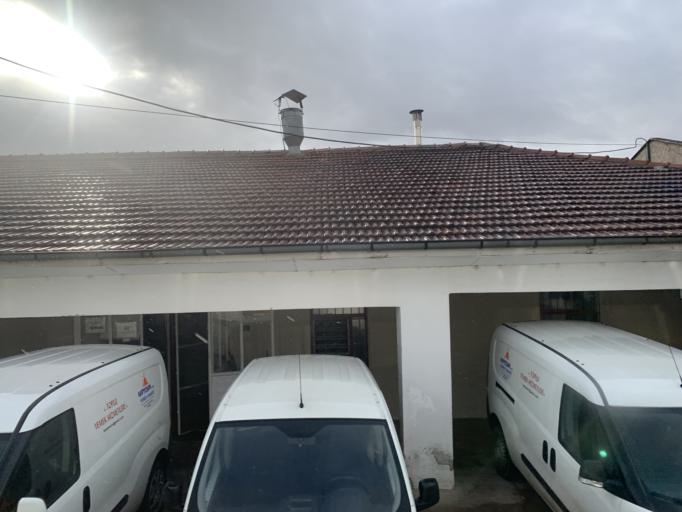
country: TR
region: Nevsehir
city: Avanos
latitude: 38.7205
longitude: 34.8570
